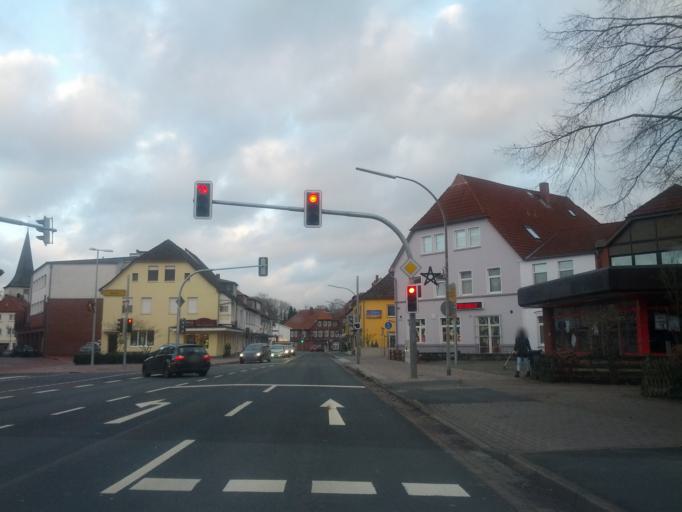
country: DE
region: Lower Saxony
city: Scheessel
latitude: 53.1676
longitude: 9.4810
